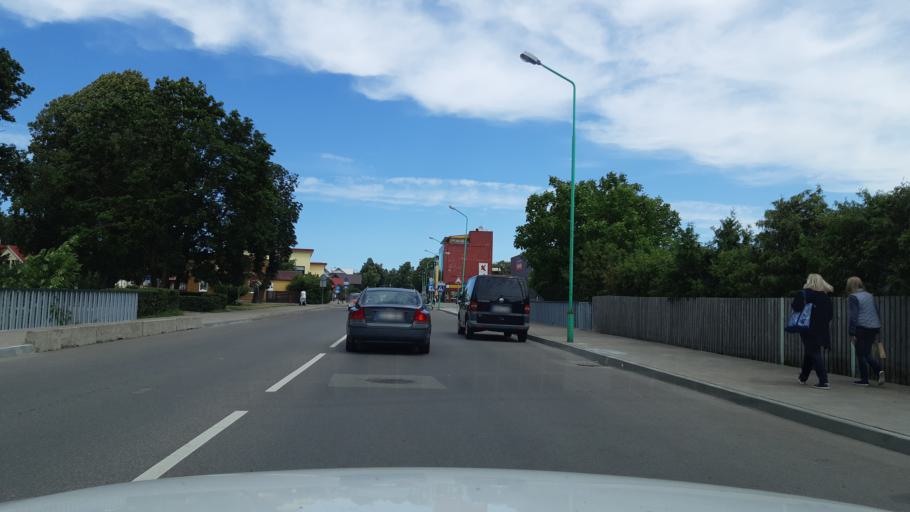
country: LT
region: Klaipedos apskritis
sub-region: Klaipeda
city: Palanga
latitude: 55.9146
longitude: 21.0689
